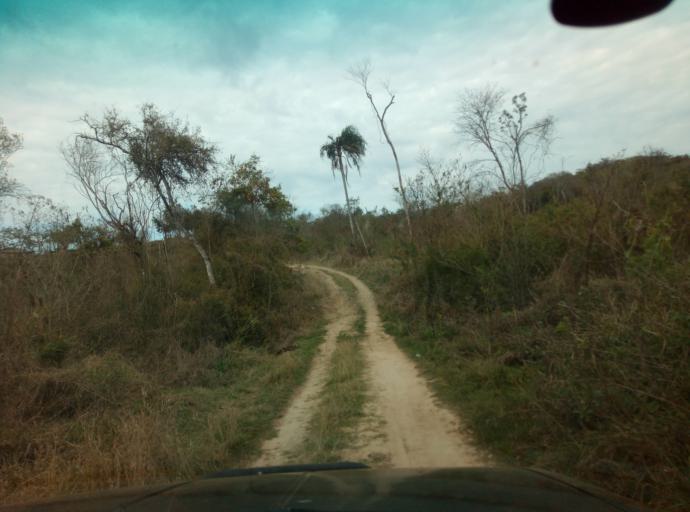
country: PY
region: Caaguazu
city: Doctor Cecilio Baez
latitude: -25.1990
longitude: -56.1264
